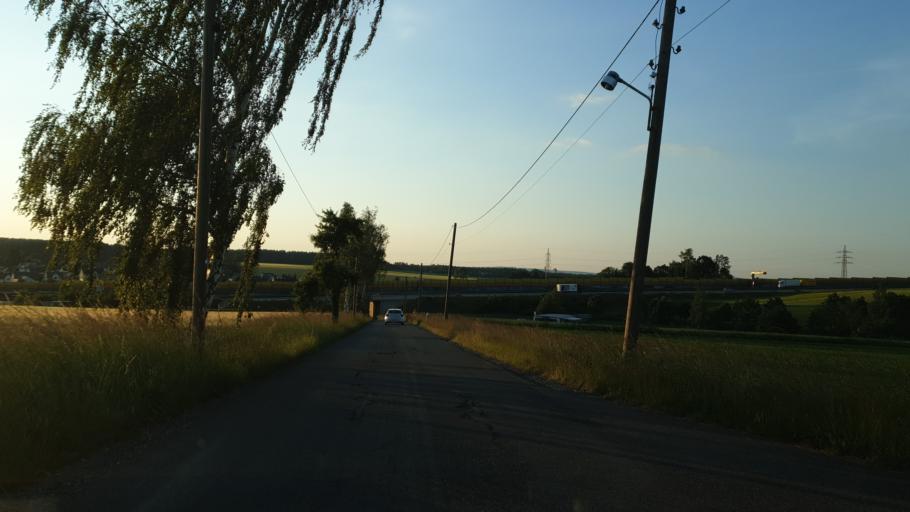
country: DE
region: Saxony
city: Oelsnitz
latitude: 50.6923
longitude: 12.7292
